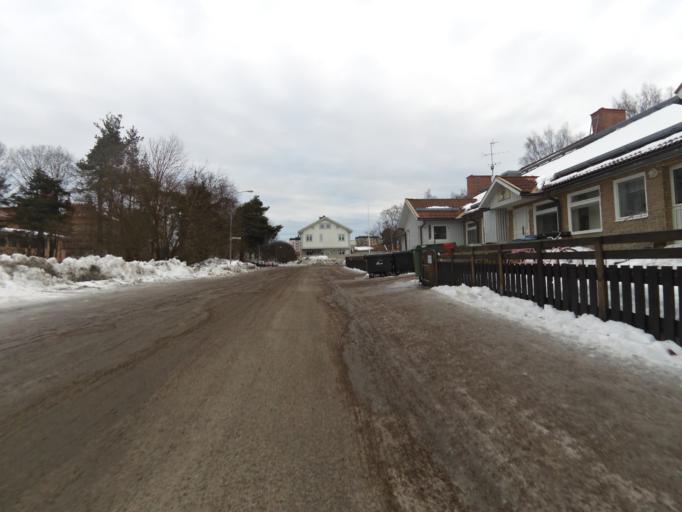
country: SE
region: Gaevleborg
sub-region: Gavle Kommun
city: Gavle
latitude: 60.6667
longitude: 17.1415
